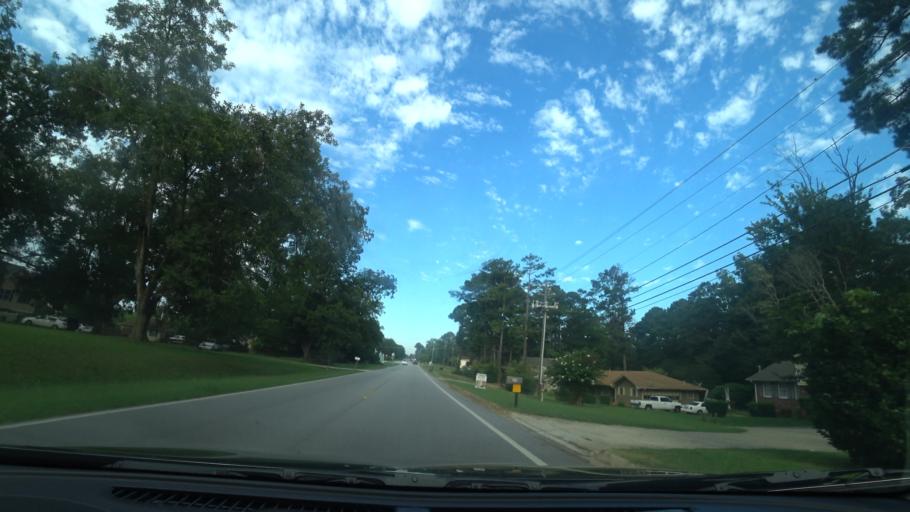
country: US
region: Georgia
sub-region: Newton County
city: Oakwood
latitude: 33.6124
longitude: -83.9640
